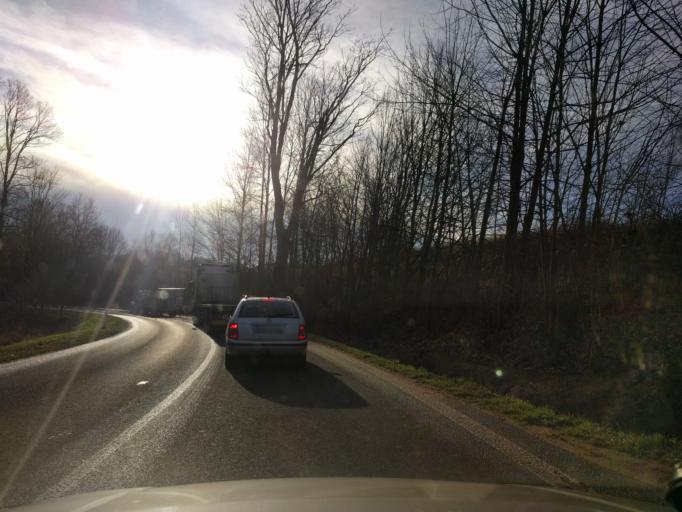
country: CZ
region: Liberecky
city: Mnisek
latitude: 50.8412
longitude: 15.0360
